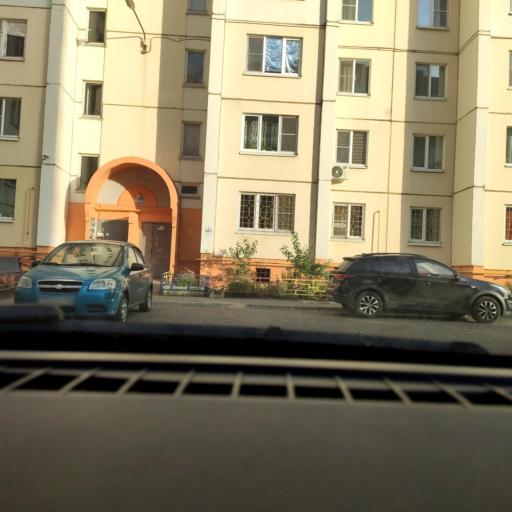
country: RU
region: Voronezj
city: Podgornoye
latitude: 51.7316
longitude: 39.2034
